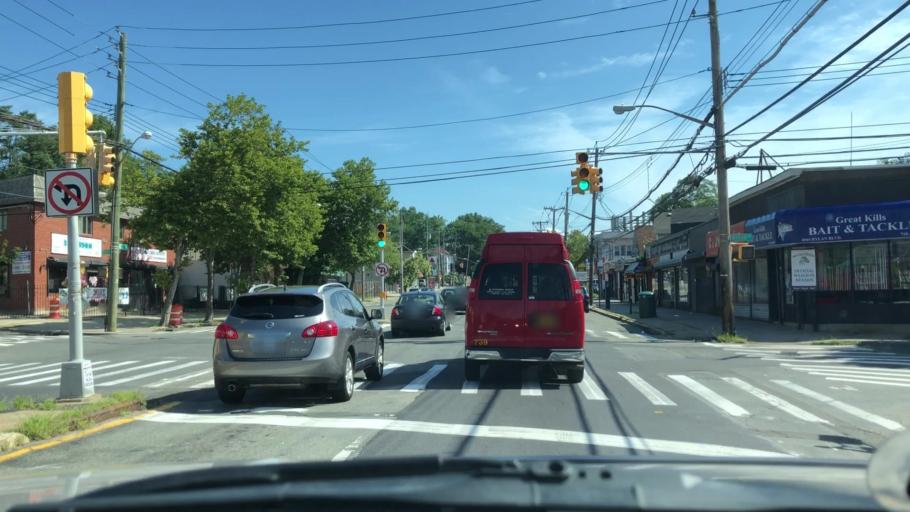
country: US
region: New York
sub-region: Richmond County
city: Staten Island
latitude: 40.5408
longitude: -74.1472
